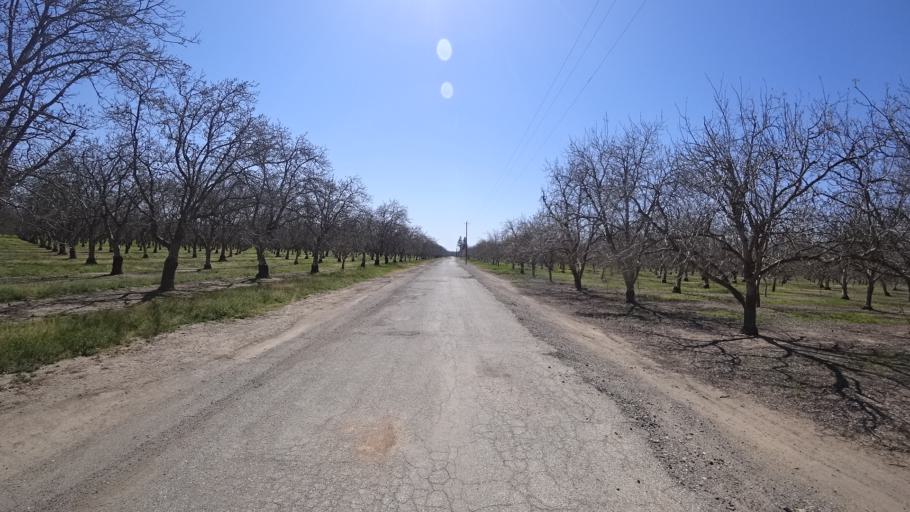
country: US
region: California
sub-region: Glenn County
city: Willows
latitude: 39.4470
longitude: -121.9869
